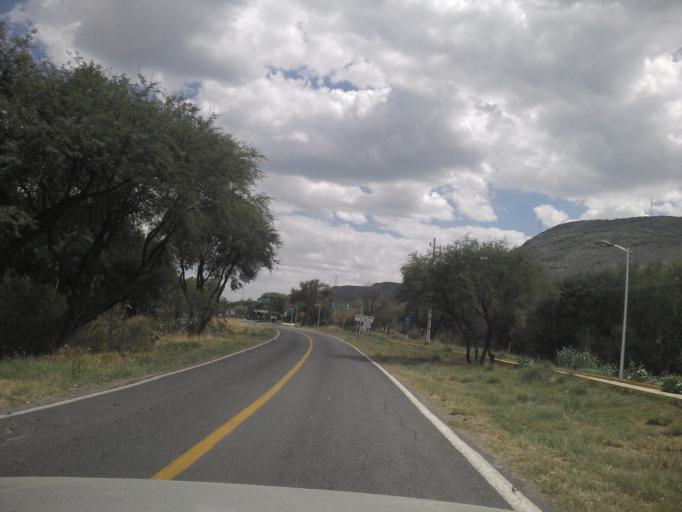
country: MX
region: Guanajuato
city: San Francisco del Rincon
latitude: 21.0265
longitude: -101.8909
